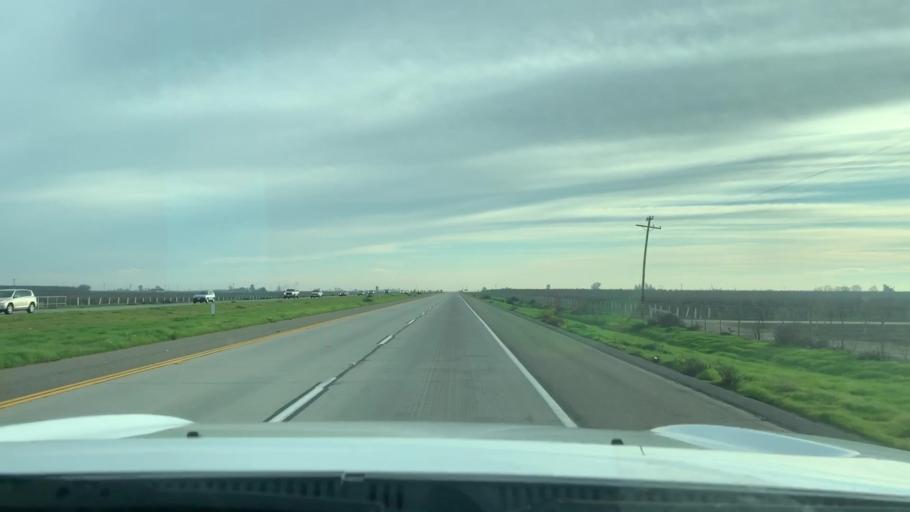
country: US
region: California
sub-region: Fresno County
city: Caruthers
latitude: 36.5841
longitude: -119.7862
